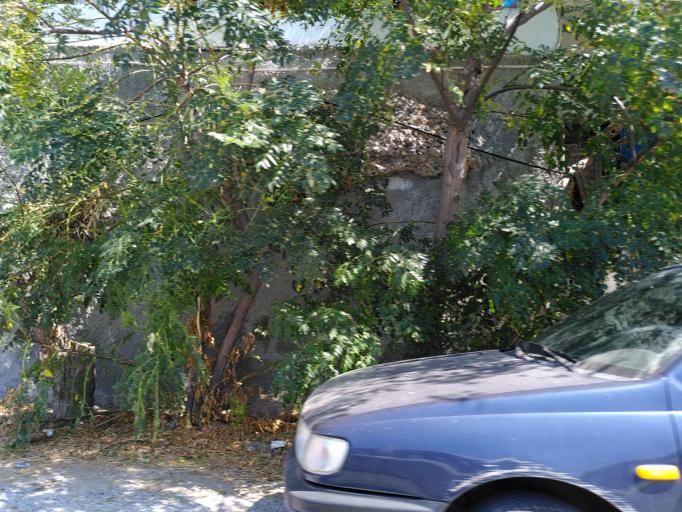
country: GR
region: South Aegean
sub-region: Nomos Kykladon
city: Amorgos
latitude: 36.9008
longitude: 25.9761
